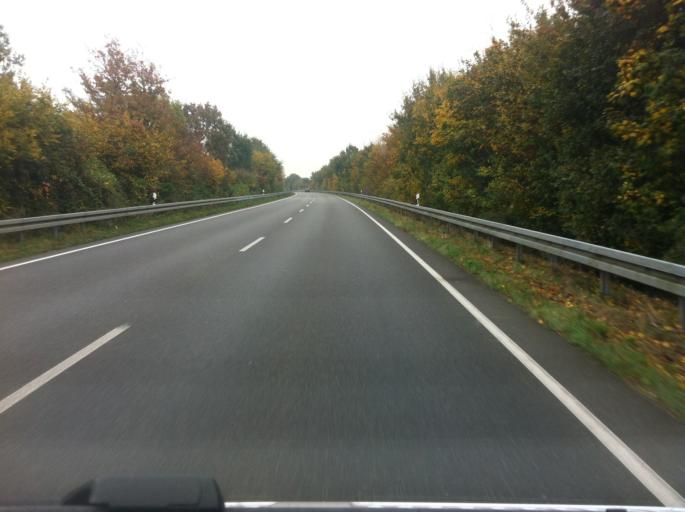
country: DE
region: North Rhine-Westphalia
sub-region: Regierungsbezirk Munster
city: Sudlohn
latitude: 51.9244
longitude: 6.8617
